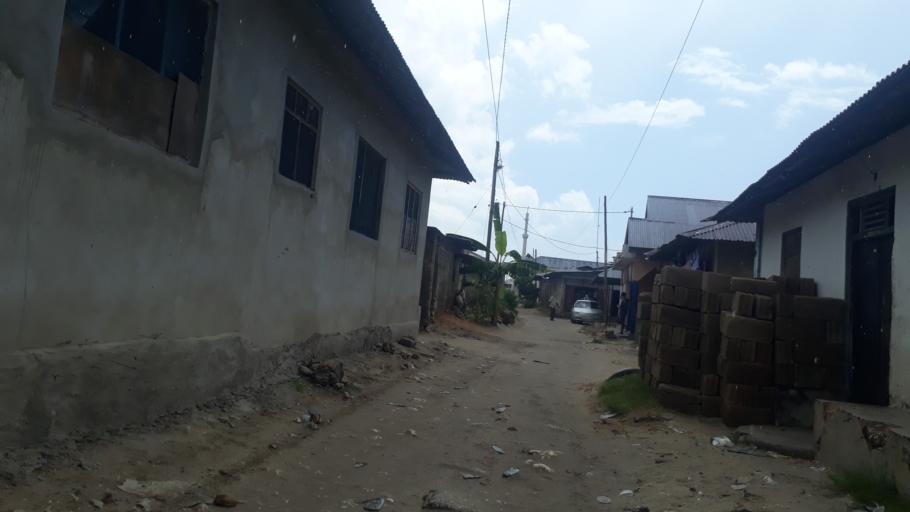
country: TZ
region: Zanzibar Urban/West
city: Zanzibar
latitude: -6.1777
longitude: 39.2098
